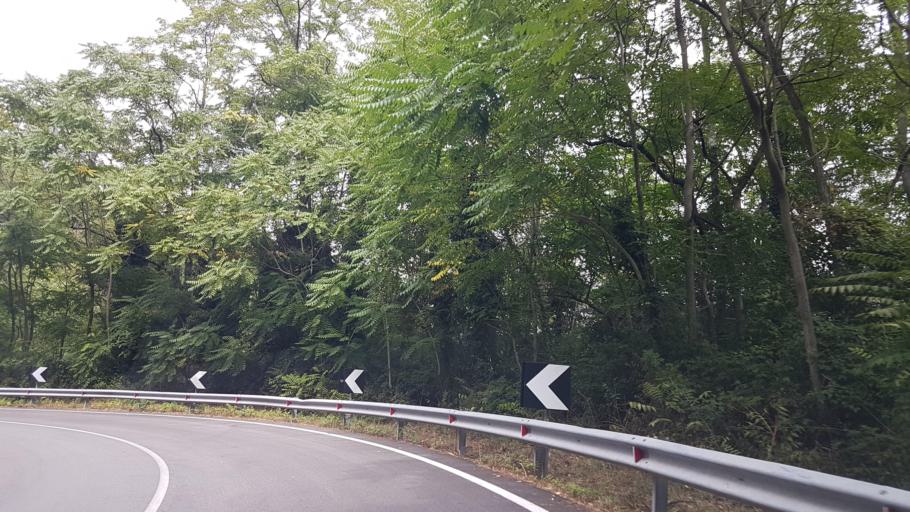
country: IT
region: Liguria
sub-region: Provincia di Genova
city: Casarza Ligure
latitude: 44.2567
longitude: 9.4627
